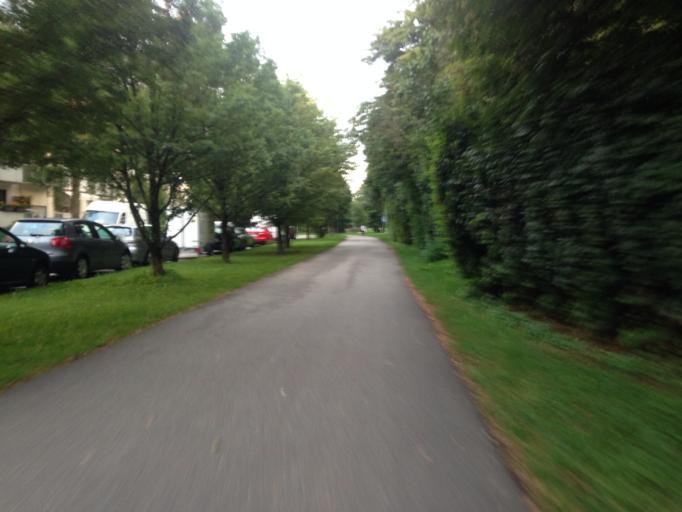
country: DE
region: Bavaria
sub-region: Upper Bavaria
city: Munich
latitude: 48.1814
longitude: 11.5755
